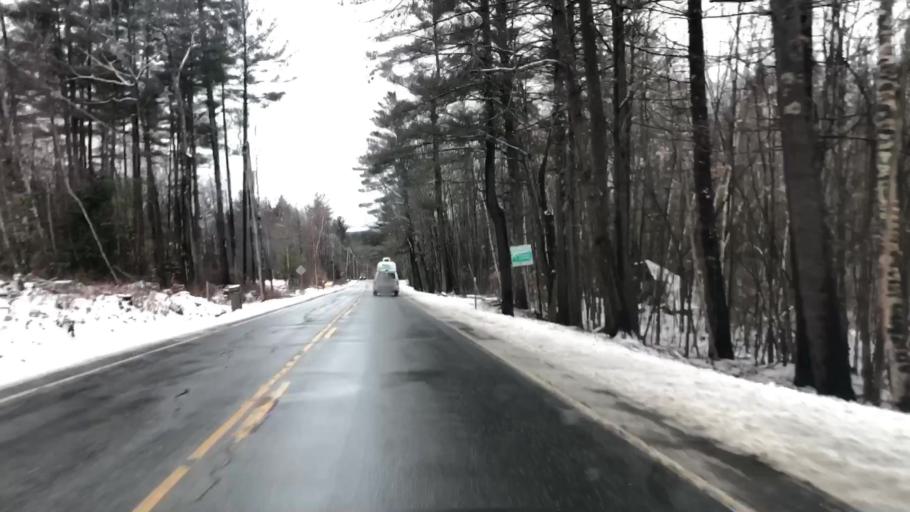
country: US
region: New Hampshire
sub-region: Hillsborough County
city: New Boston
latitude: 43.0135
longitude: -71.6862
